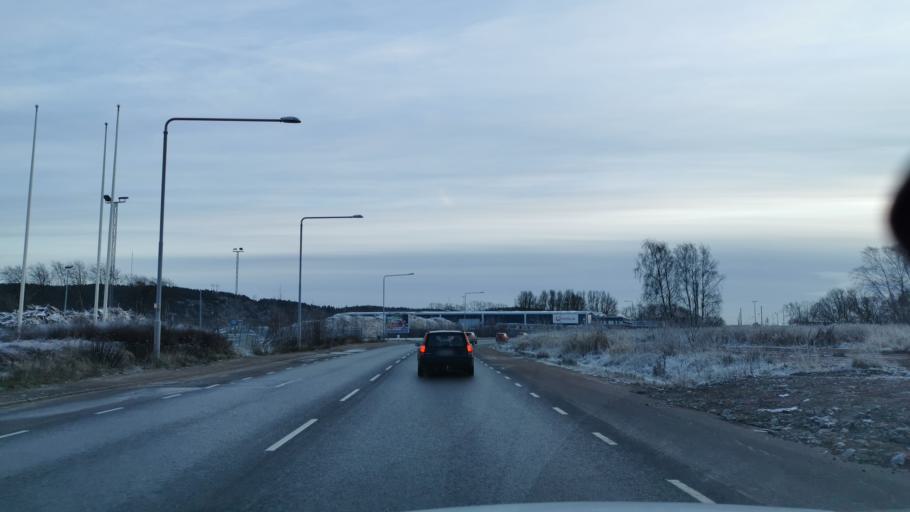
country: SE
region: Vaestra Goetaland
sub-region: Goteborg
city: Hammarkullen
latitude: 57.7603
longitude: 11.9948
